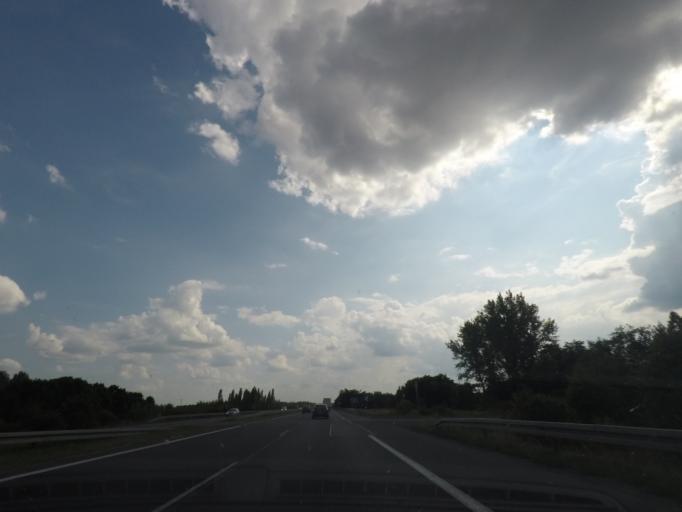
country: PL
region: Lodz Voivodeship
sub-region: Powiat radomszczanski
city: Kamiensk
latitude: 51.2666
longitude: 19.5304
